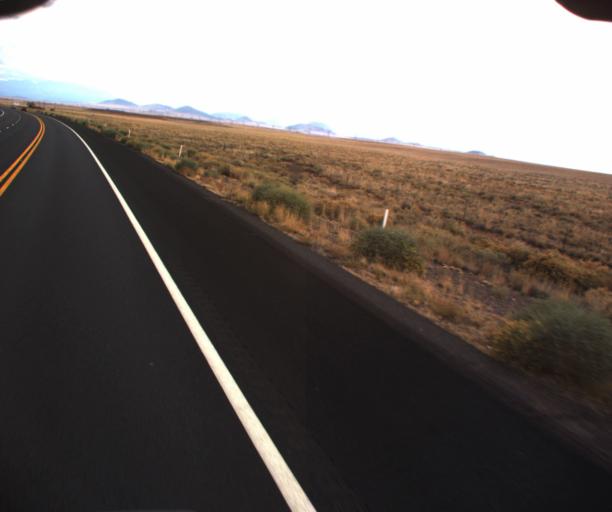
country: US
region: Arizona
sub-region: Coconino County
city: Flagstaff
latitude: 35.6917
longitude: -111.5039
